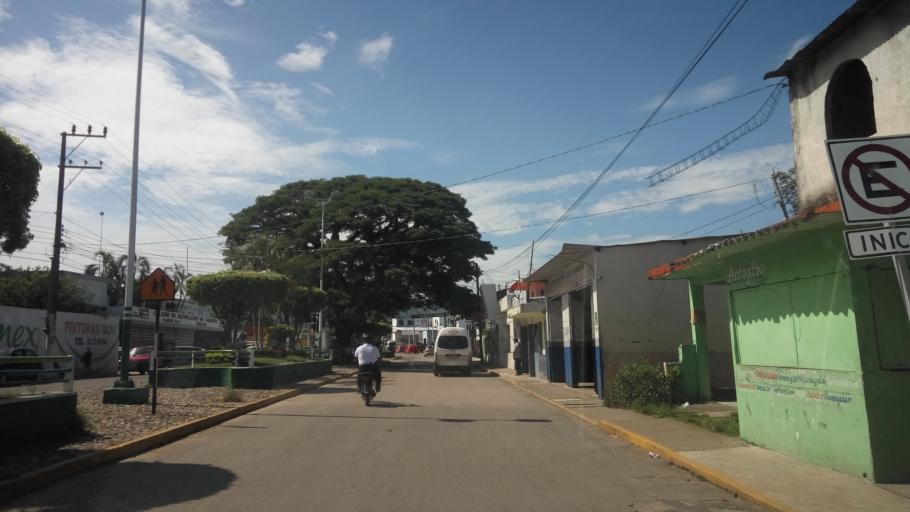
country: MX
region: Tabasco
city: Teapa
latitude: 17.5621
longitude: -92.9503
